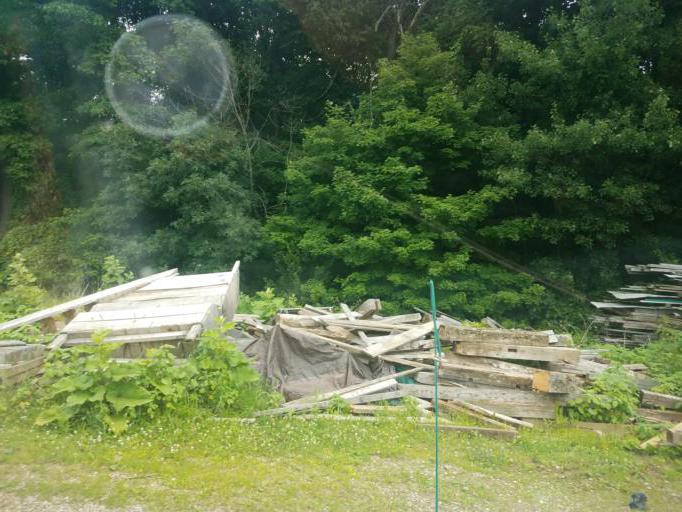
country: US
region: Ohio
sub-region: Sandusky County
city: Bellville
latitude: 40.5765
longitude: -82.4811
